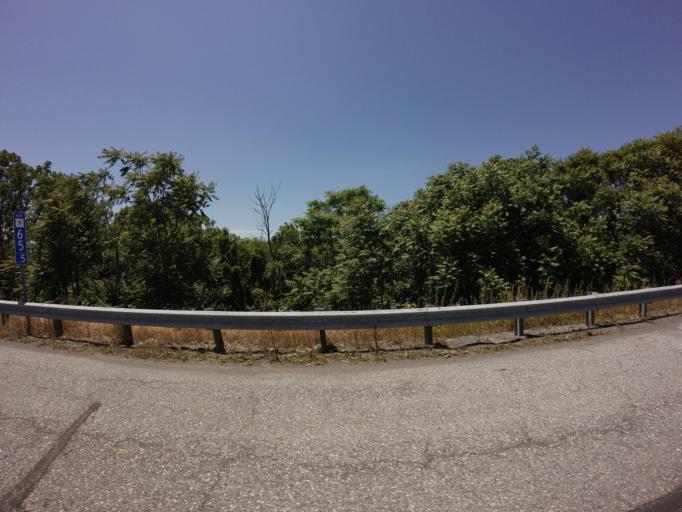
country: US
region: West Virginia
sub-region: Jefferson County
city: Ranson
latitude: 39.3098
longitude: -77.8433
